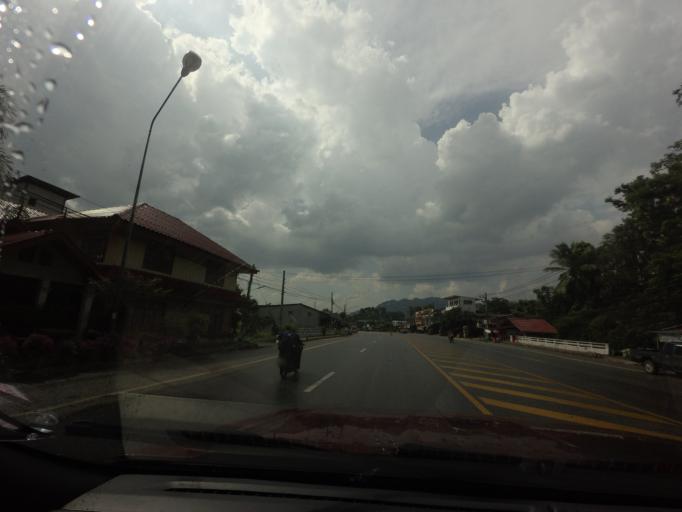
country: TH
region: Yala
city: Krong Pi Nang
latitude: 6.4129
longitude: 101.2800
